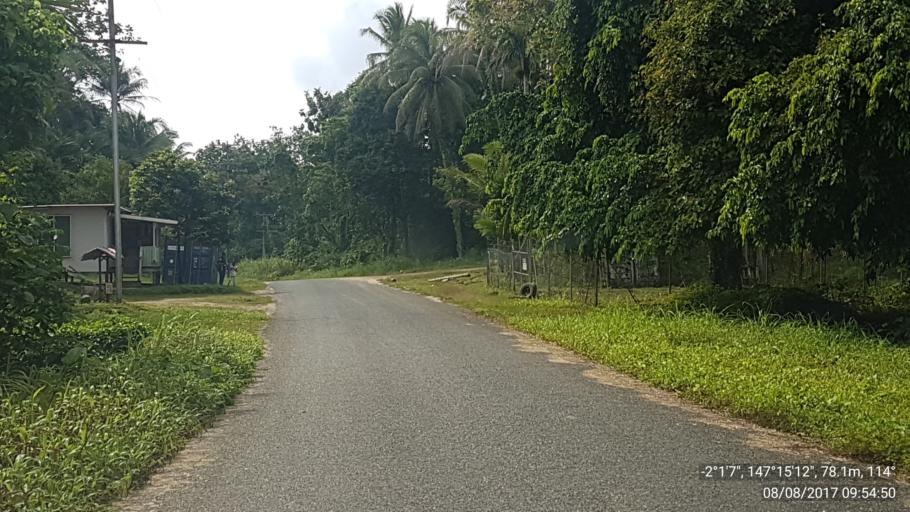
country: PG
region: Manus
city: Lorengau
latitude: -2.0186
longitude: 147.2536
